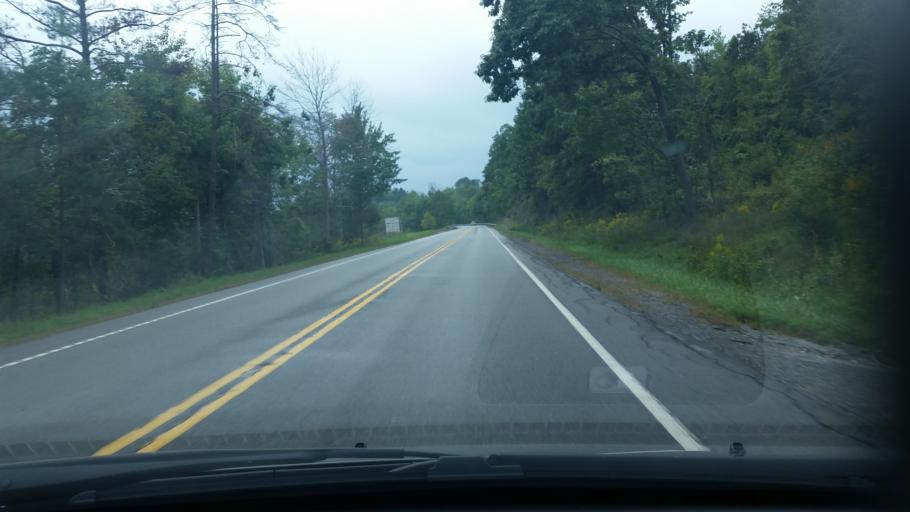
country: US
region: Pennsylvania
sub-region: Clearfield County
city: Shiloh
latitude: 41.0824
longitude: -78.2773
